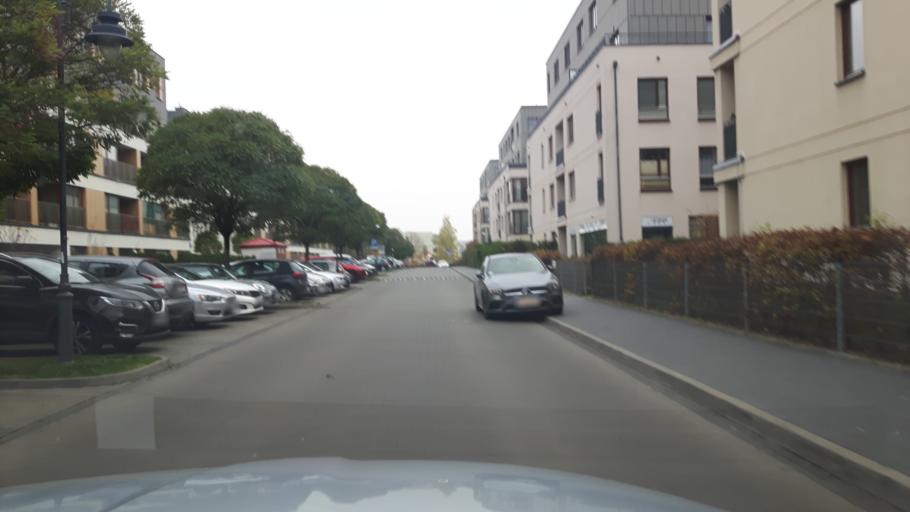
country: PL
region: Masovian Voivodeship
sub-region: Warszawa
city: Ursynow
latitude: 52.1598
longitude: 21.0669
